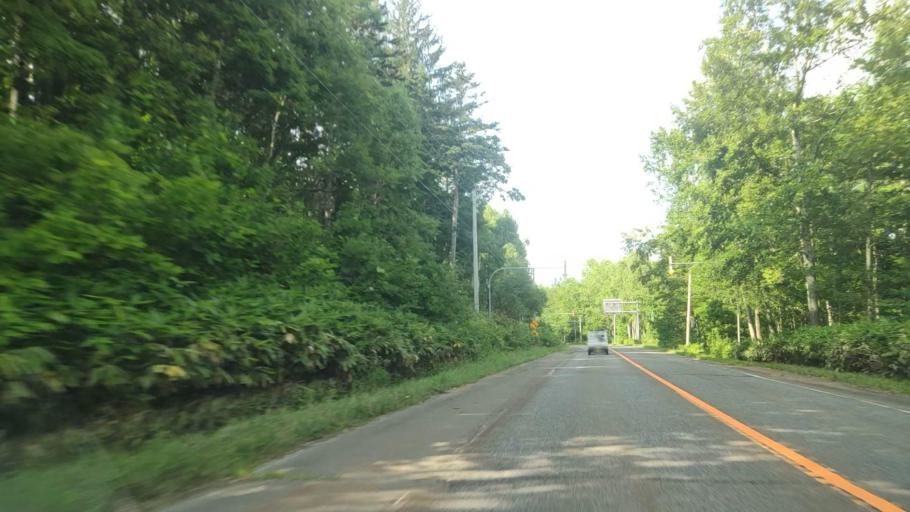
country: JP
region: Hokkaido
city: Nayoro
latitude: 44.3880
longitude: 142.3977
